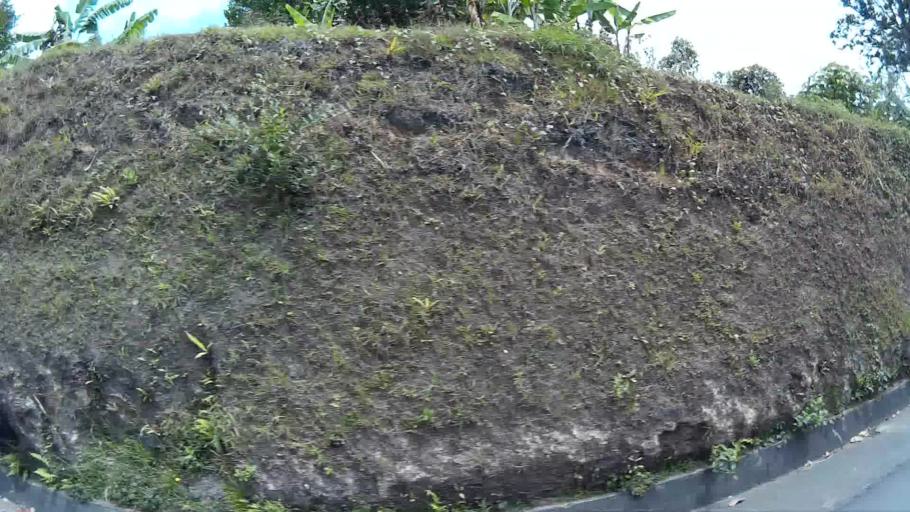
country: CO
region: Quindio
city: Circasia
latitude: 4.5923
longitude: -75.6409
